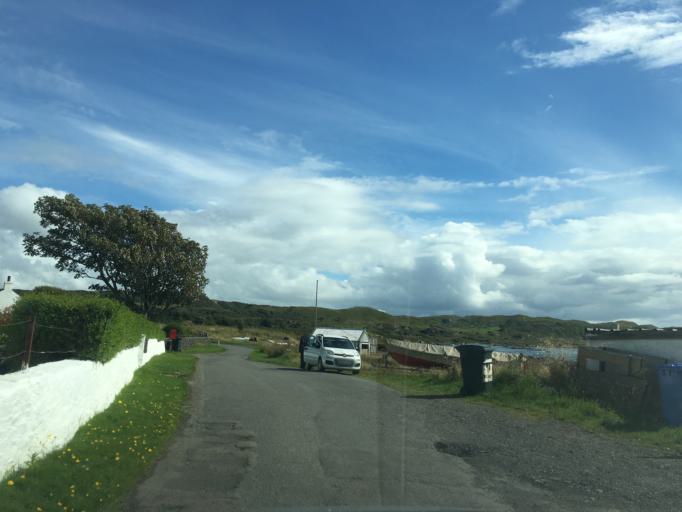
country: GB
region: Scotland
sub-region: Argyll and Bute
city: Isle Of Mull
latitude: 56.2501
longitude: -5.6541
